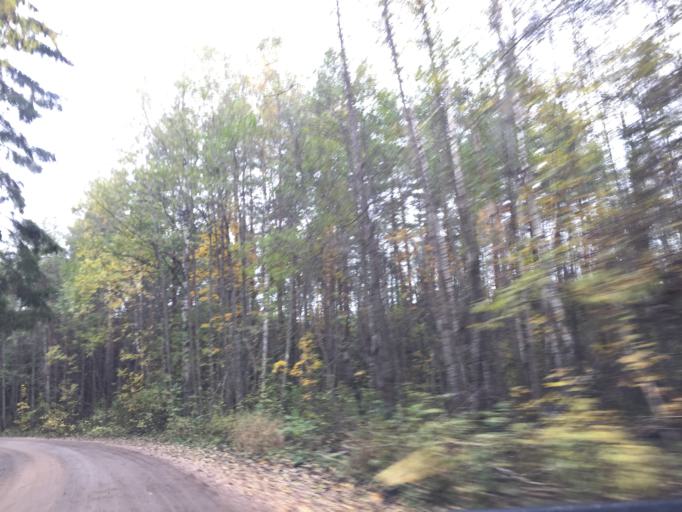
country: LV
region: Salacgrivas
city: Salacgriva
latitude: 57.5783
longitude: 24.3817
